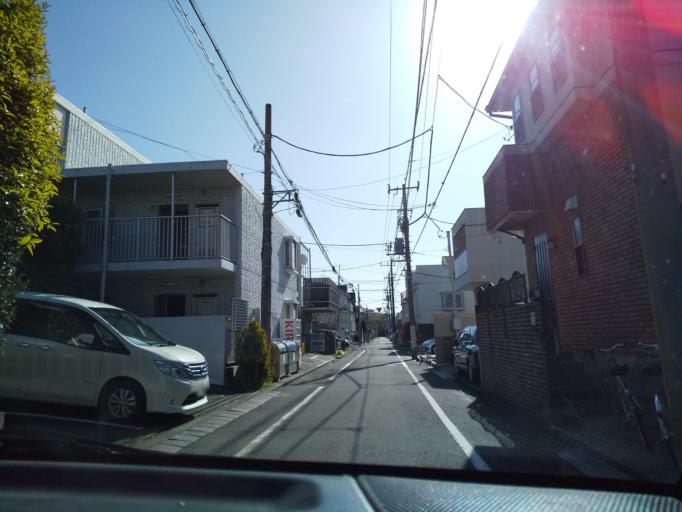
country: JP
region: Tokyo
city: Kokubunji
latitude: 35.6935
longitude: 139.4387
